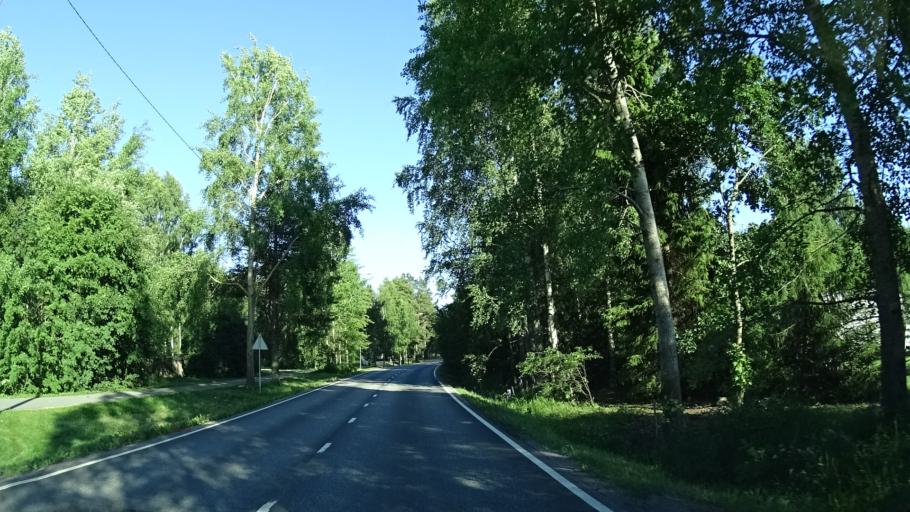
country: FI
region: Satakunta
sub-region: Pori
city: Nakkila
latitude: 61.3722
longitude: 22.0379
